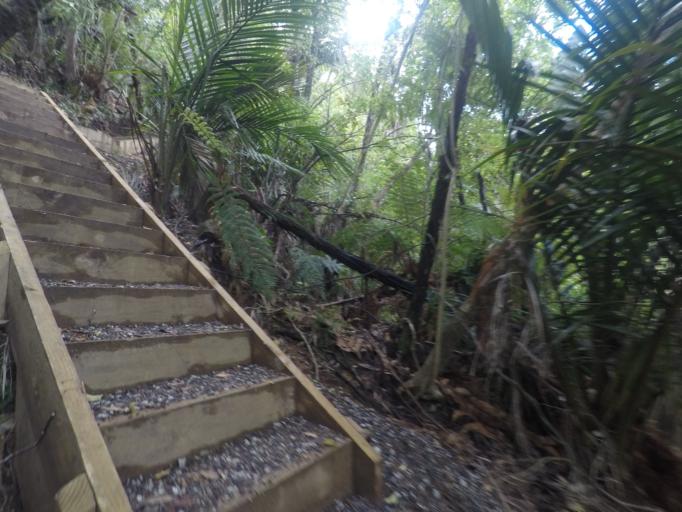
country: NZ
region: Auckland
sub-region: Auckland
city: Titirangi
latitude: -37.0002
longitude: 174.5444
